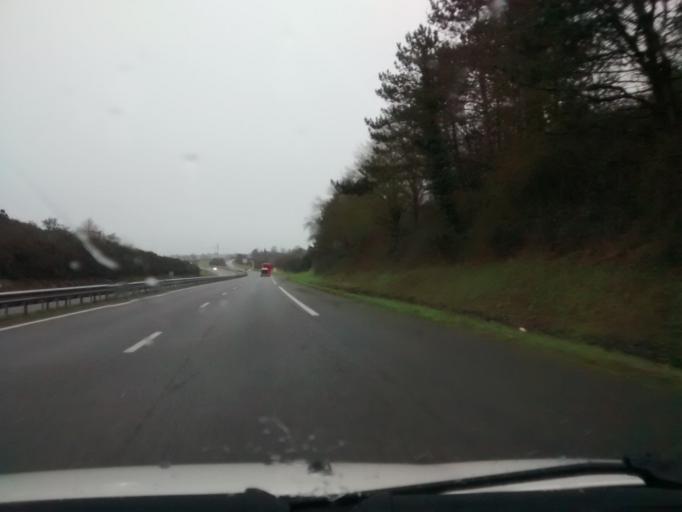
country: FR
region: Brittany
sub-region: Departement d'Ille-et-Vilaine
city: Liffre
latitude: 48.2167
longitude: -1.5111
